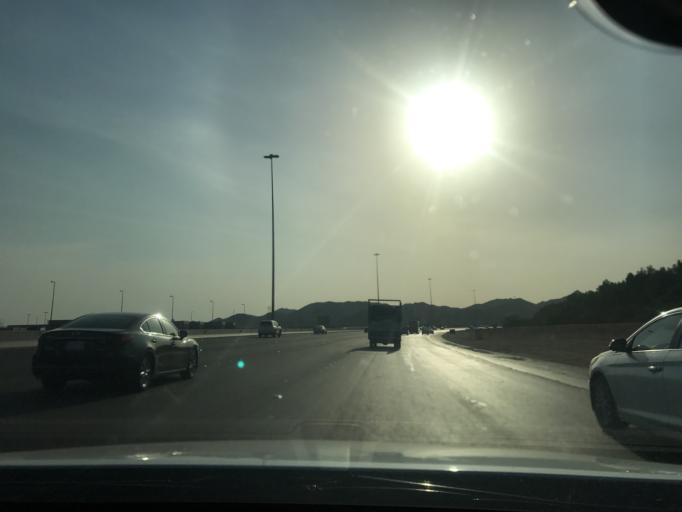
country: SA
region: Makkah
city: Jeddah
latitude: 21.3893
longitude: 39.4217
